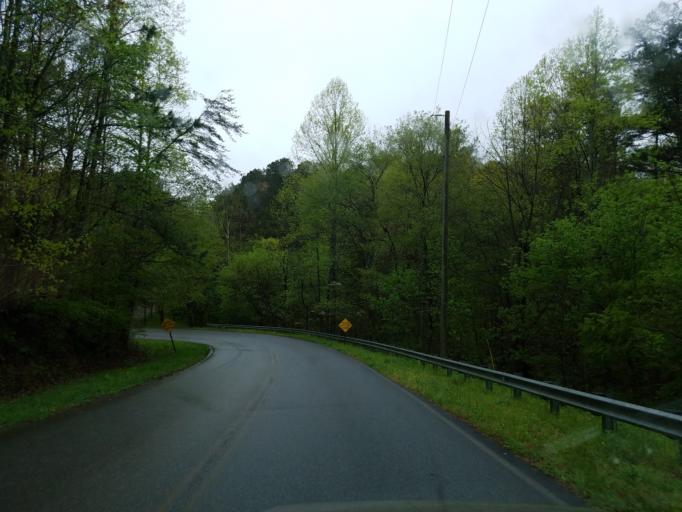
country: US
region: Georgia
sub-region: Gilmer County
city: Ellijay
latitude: 34.5669
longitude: -84.5227
